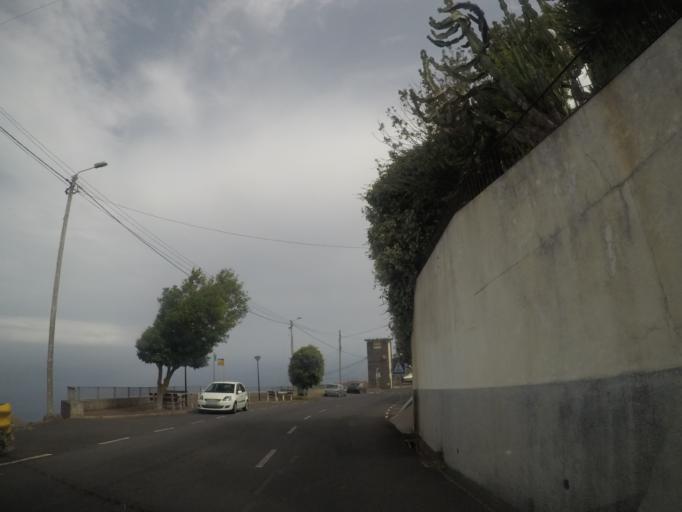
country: PT
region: Madeira
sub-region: Santa Cruz
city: Santa Cruz
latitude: 32.6744
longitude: -16.8182
